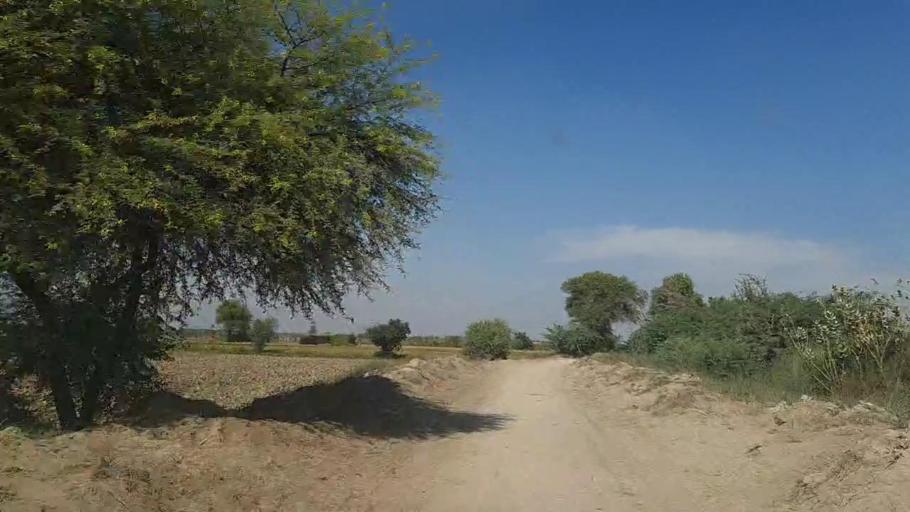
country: PK
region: Sindh
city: Mirpur Batoro
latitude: 24.7527
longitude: 68.2867
